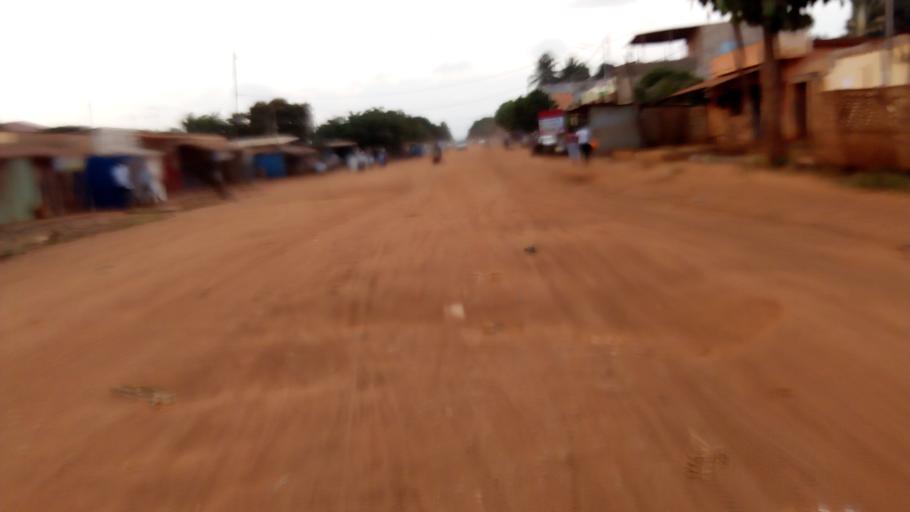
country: TG
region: Maritime
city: Lome
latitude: 6.2314
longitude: 1.1936
